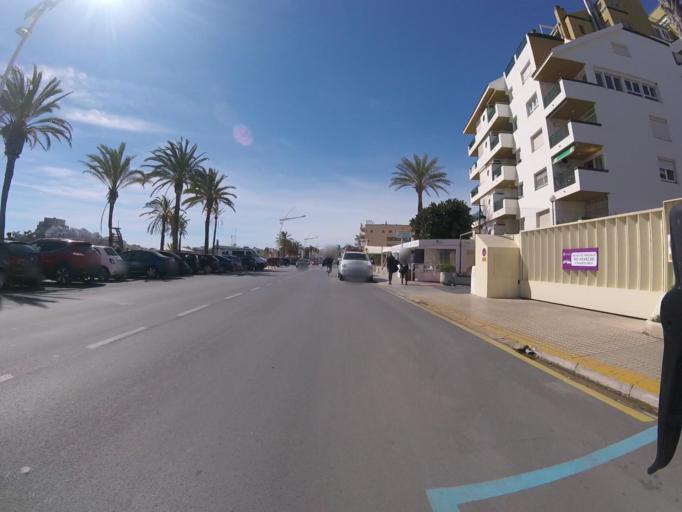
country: ES
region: Valencia
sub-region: Provincia de Castello
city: Peniscola
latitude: 40.3636
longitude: 0.4027
